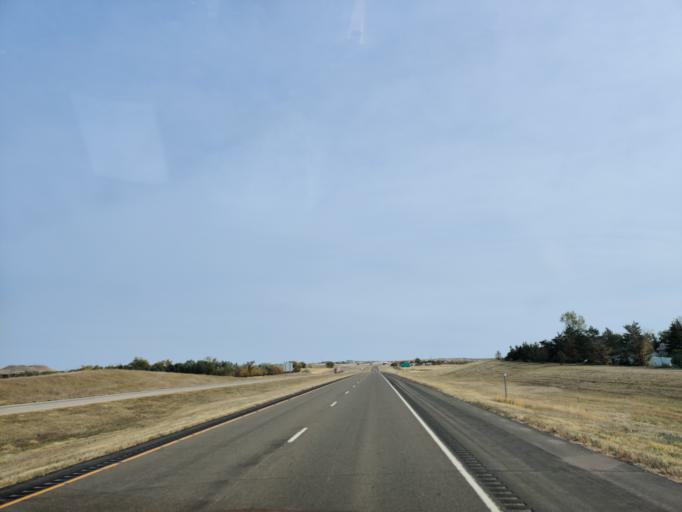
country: US
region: North Dakota
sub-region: Stark County
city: Dickinson
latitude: 46.8942
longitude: -102.7663
